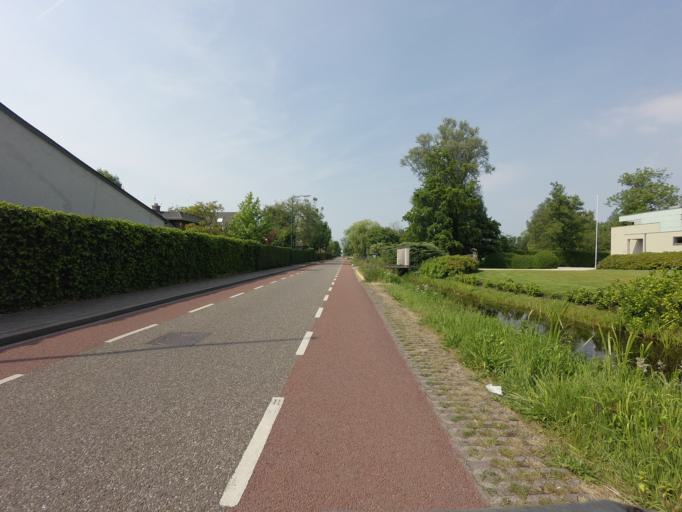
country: NL
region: North Holland
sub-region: Gemeente Wijdemeren
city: Oud-Loosdrecht
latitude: 52.1793
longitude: 5.0691
